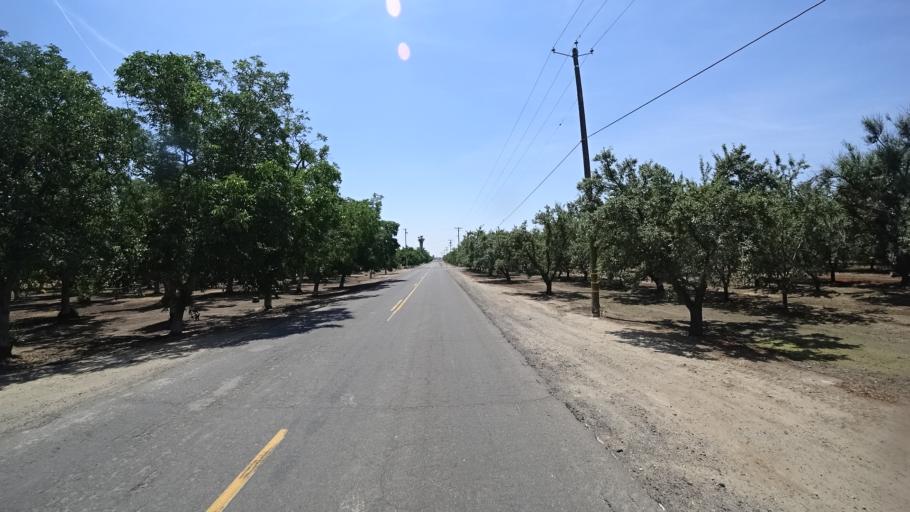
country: US
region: California
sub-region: Fresno County
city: Riverdale
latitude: 36.3958
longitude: -119.8094
